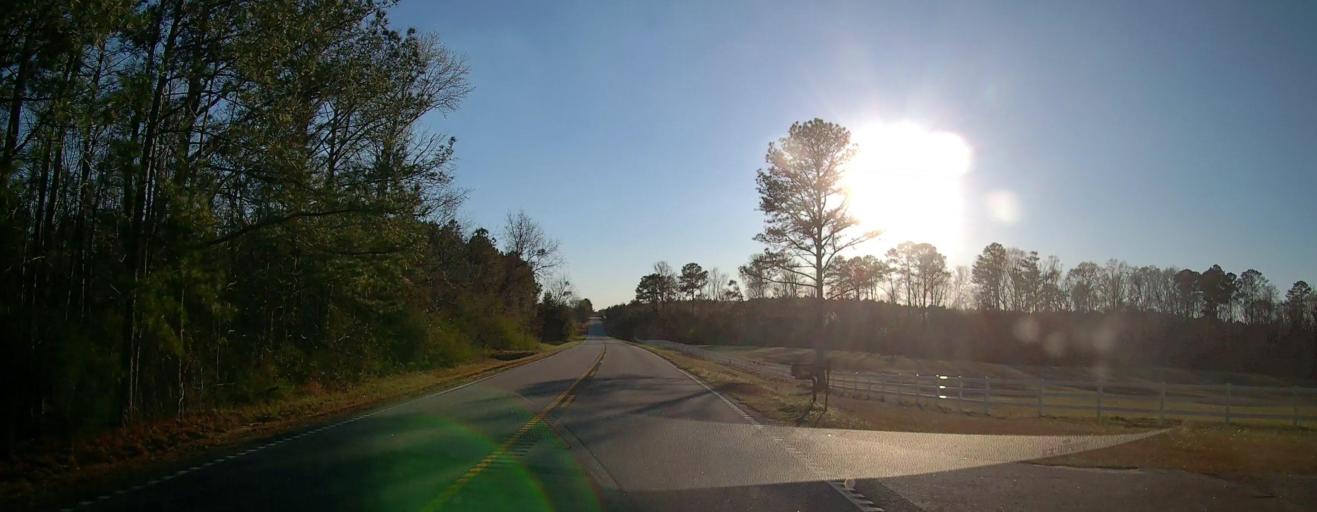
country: US
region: Georgia
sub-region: Talbot County
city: Sardis
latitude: 32.6418
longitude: -84.7100
